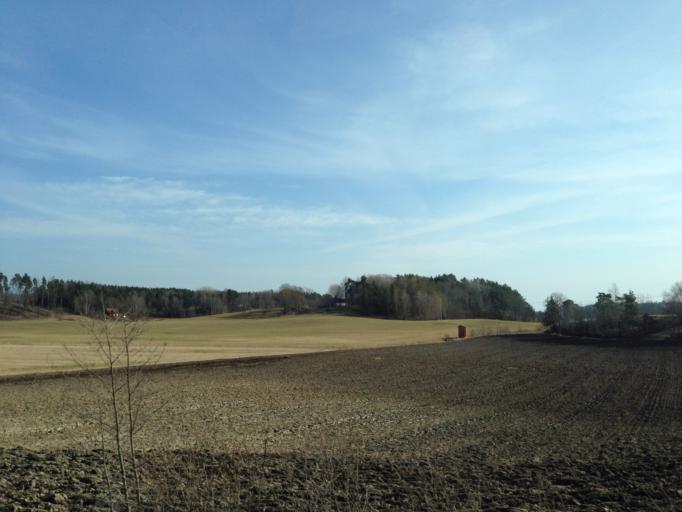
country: SE
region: Soedermanland
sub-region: Strangnas Kommun
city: Akers Styckebruk
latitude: 59.0757
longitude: 16.9534
